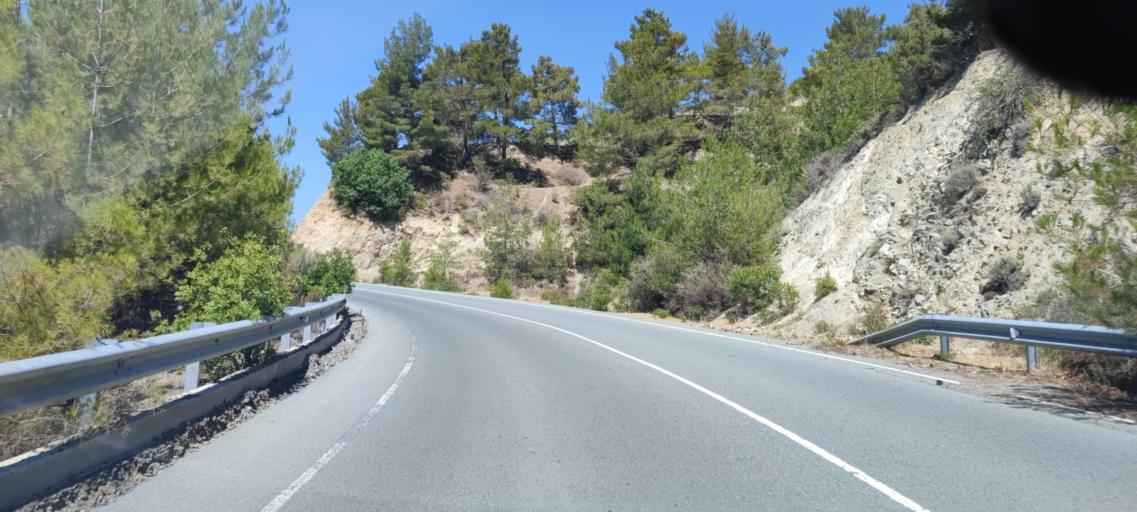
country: CY
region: Limassol
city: Pachna
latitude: 34.8994
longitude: 32.8179
